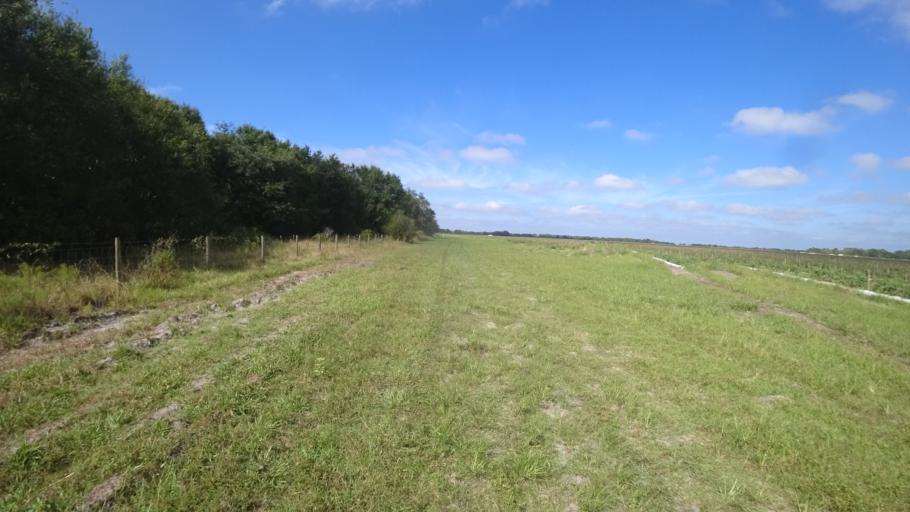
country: US
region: Florida
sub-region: DeSoto County
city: Arcadia
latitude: 27.2799
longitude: -82.0822
